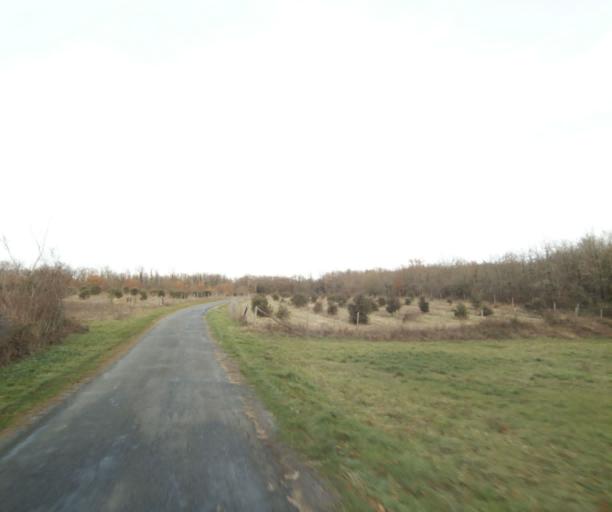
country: FR
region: Poitou-Charentes
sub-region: Departement de la Charente-Maritime
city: Fontcouverte
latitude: 45.8020
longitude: -0.5845
